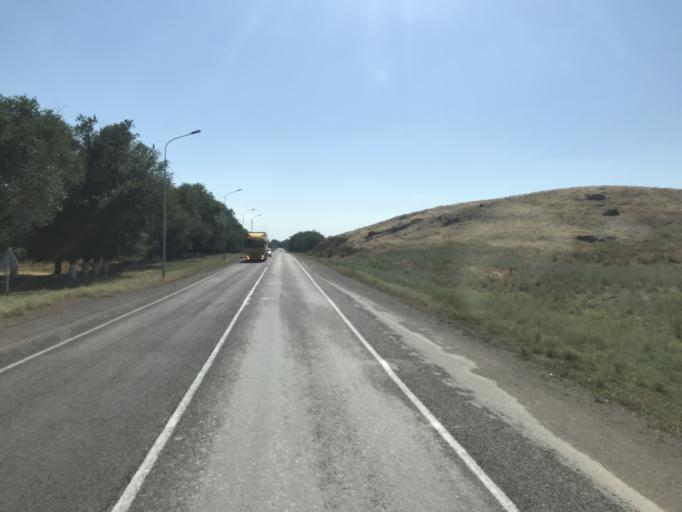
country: KZ
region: Zhambyl
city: Georgiyevka
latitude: 43.2404
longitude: 74.7740
